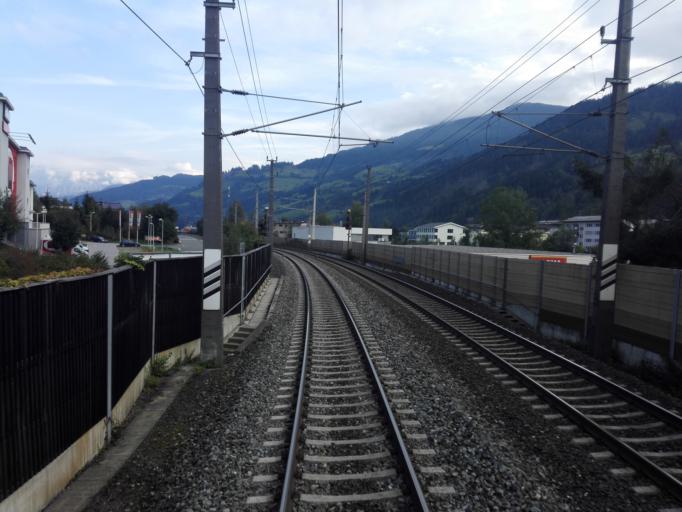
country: AT
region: Salzburg
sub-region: Politischer Bezirk Sankt Johann im Pongau
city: Sankt Johann im Pongau
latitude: 47.3562
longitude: 13.2006
